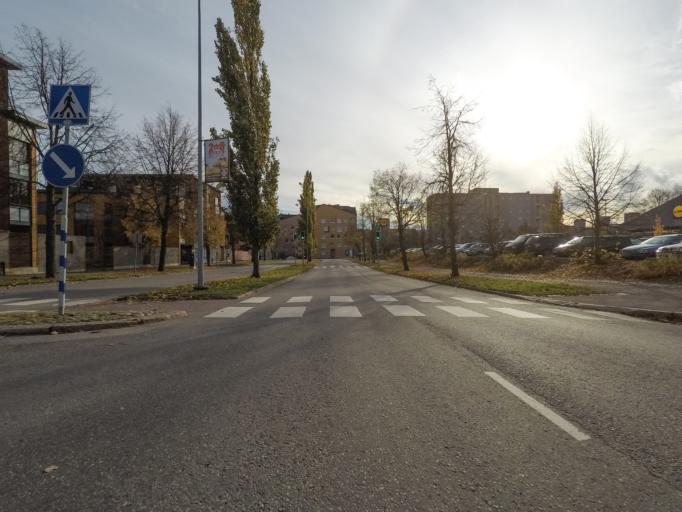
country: FI
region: Uusimaa
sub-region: Porvoo
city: Porvoo
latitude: 60.3906
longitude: 25.6527
